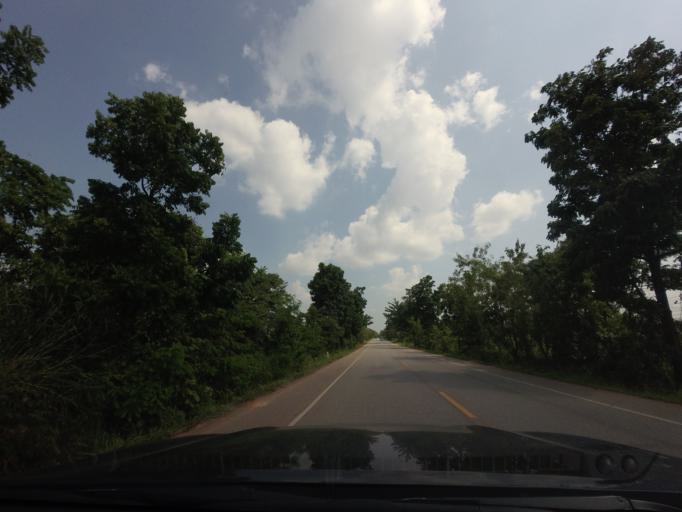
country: TH
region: Phitsanulok
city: Chat Trakan
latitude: 17.2647
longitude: 100.5519
